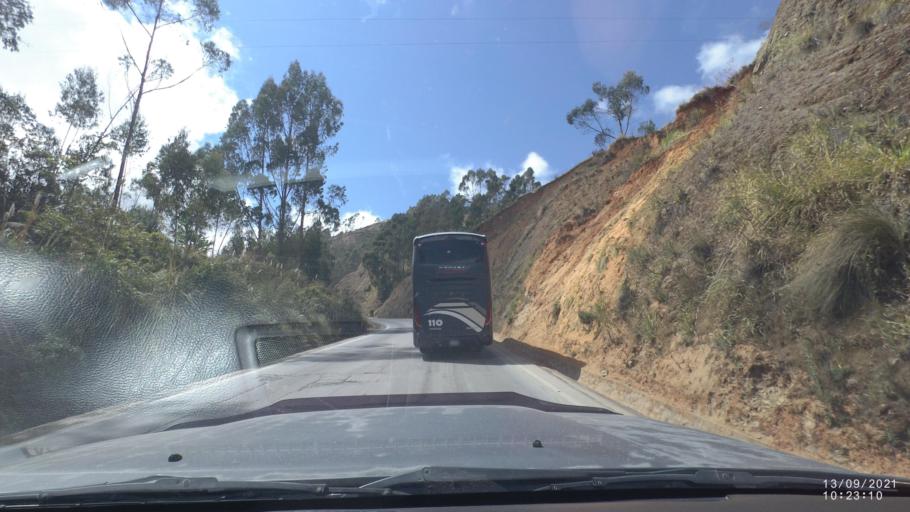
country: BO
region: Cochabamba
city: Colomi
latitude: -17.3173
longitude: -65.8691
